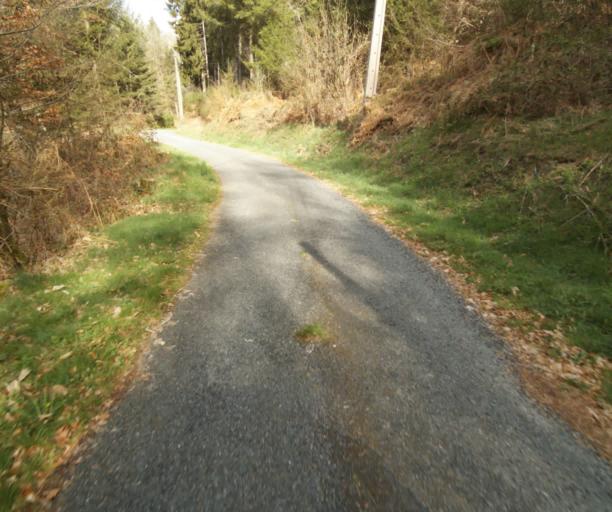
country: FR
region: Limousin
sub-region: Departement de la Correze
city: Correze
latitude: 45.3584
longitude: 1.8764
